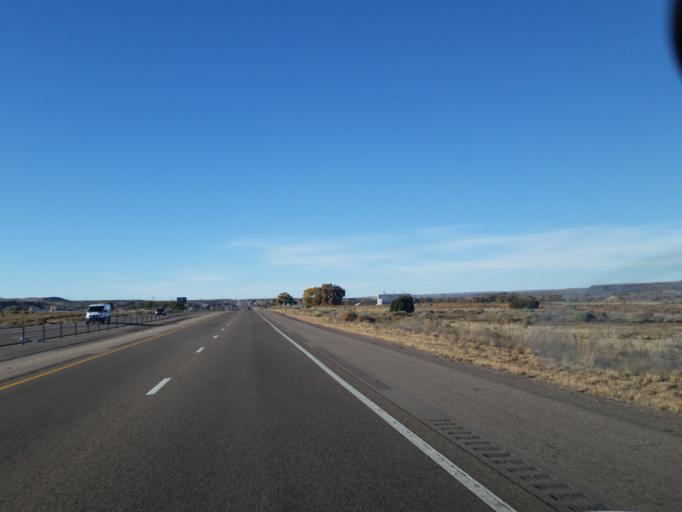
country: US
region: New Mexico
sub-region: Sandoval County
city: San Felipe Pueblo
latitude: 35.3921
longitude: -106.4525
